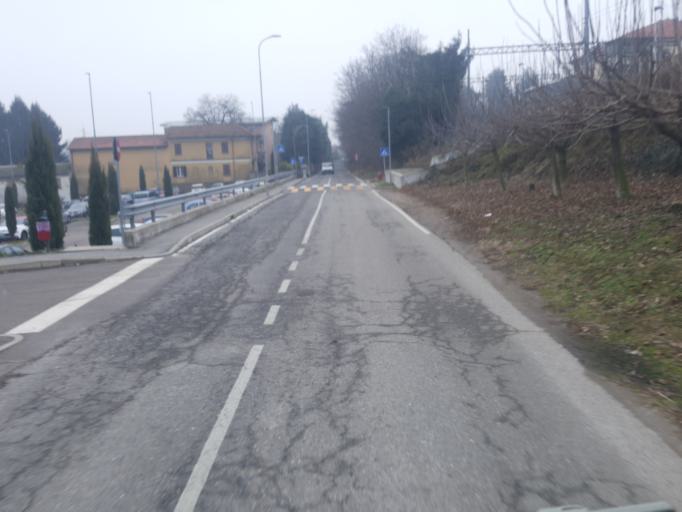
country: IT
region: Lombardy
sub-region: Provincia di Varese
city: Albizzate
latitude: 45.7241
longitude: 8.8067
